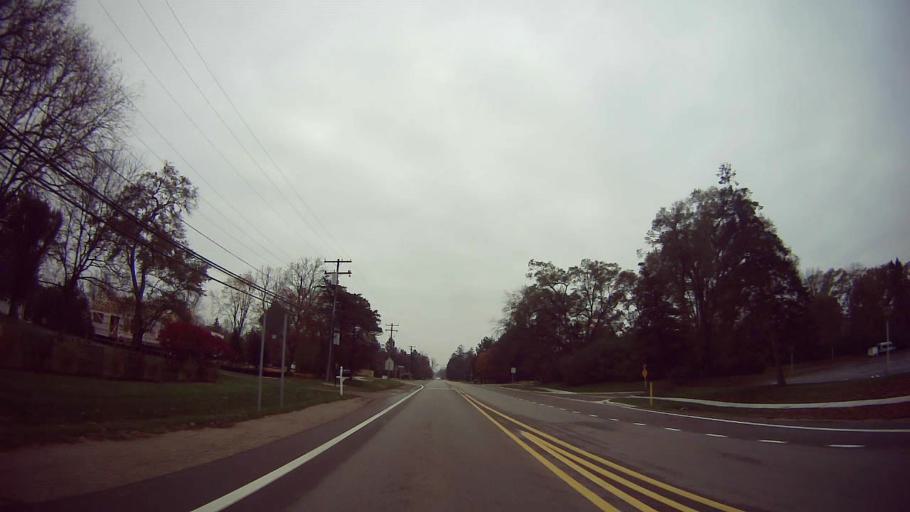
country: US
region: Michigan
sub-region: Oakland County
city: Bingham Farms
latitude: 42.5296
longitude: -83.2642
